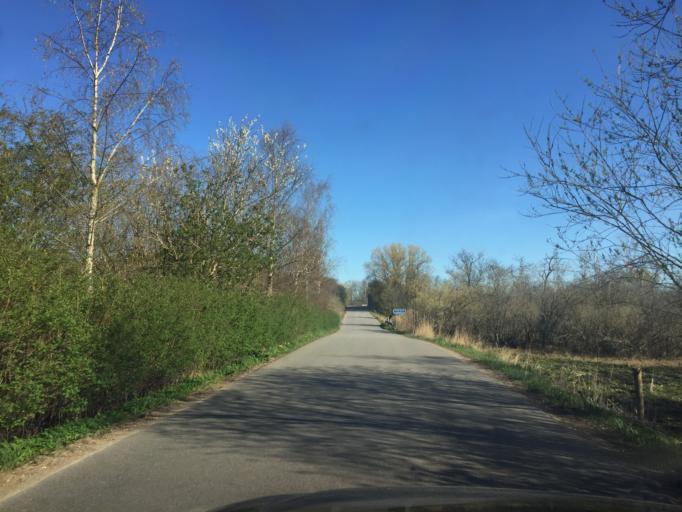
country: DK
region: Capital Region
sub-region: Egedal Kommune
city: Vekso
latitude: 55.7392
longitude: 12.2131
